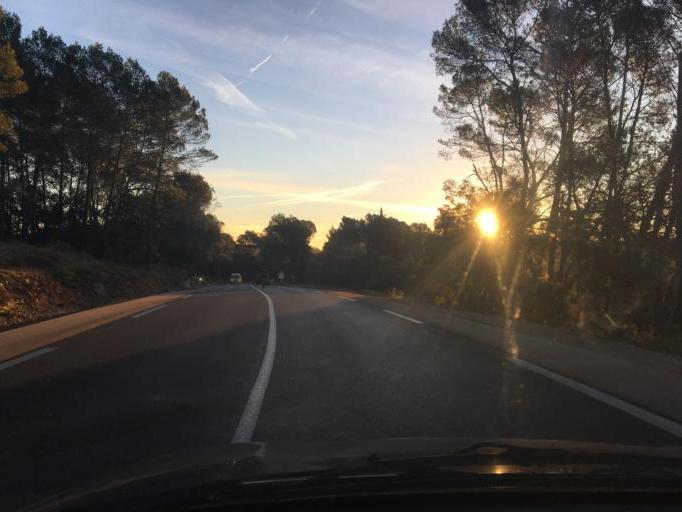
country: FR
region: Provence-Alpes-Cote d'Azur
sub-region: Departement du Var
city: Taradeau
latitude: 43.4616
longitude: 6.4042
